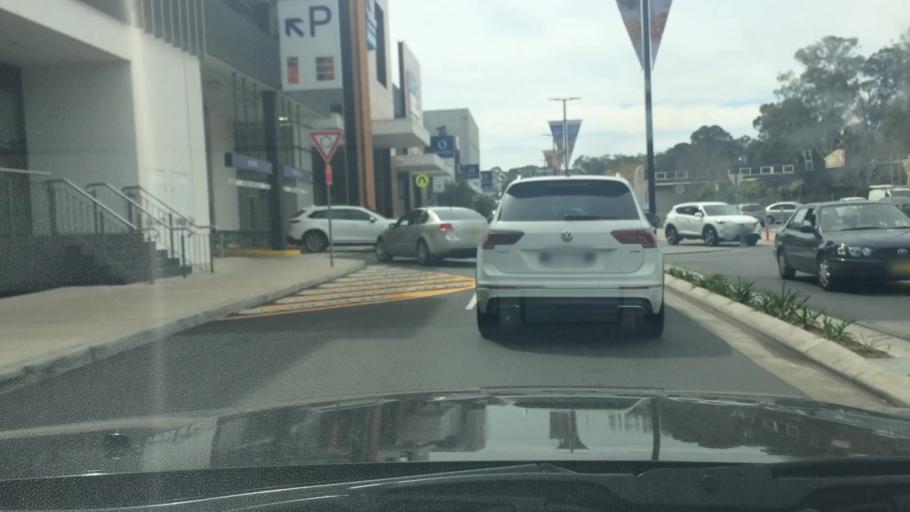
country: AU
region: New South Wales
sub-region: Fairfield
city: Cabramatta West
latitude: -33.8593
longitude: 150.8995
